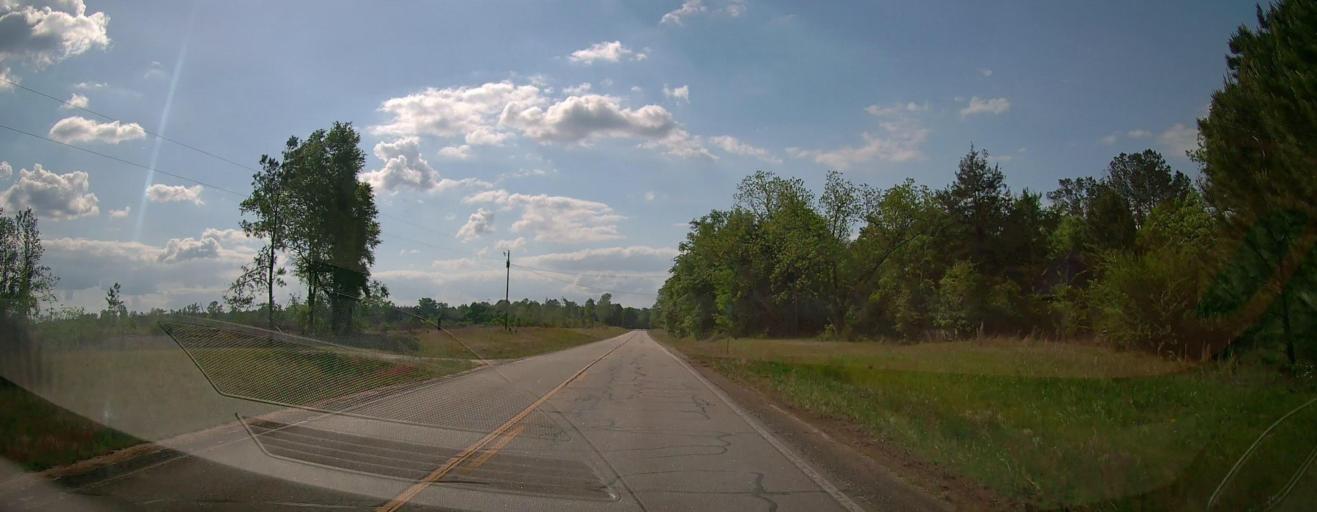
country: US
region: Georgia
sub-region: Washington County
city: Tennille
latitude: 32.9092
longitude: -82.9777
